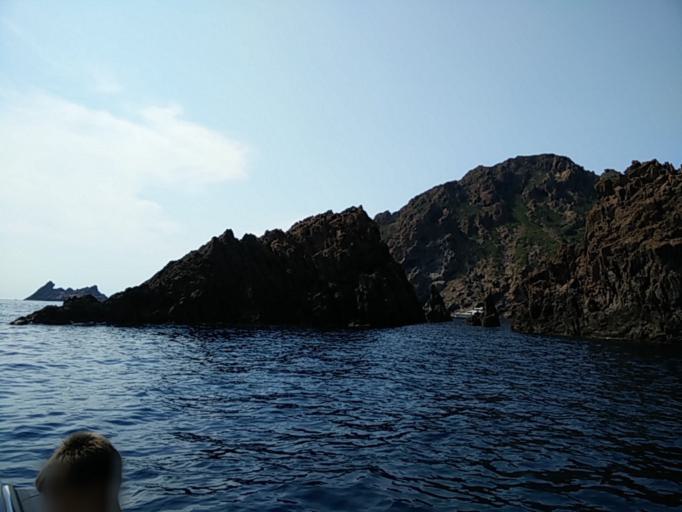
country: FR
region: Corsica
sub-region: Departement de la Corse-du-Sud
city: Cargese
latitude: 42.3615
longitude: 8.5555
